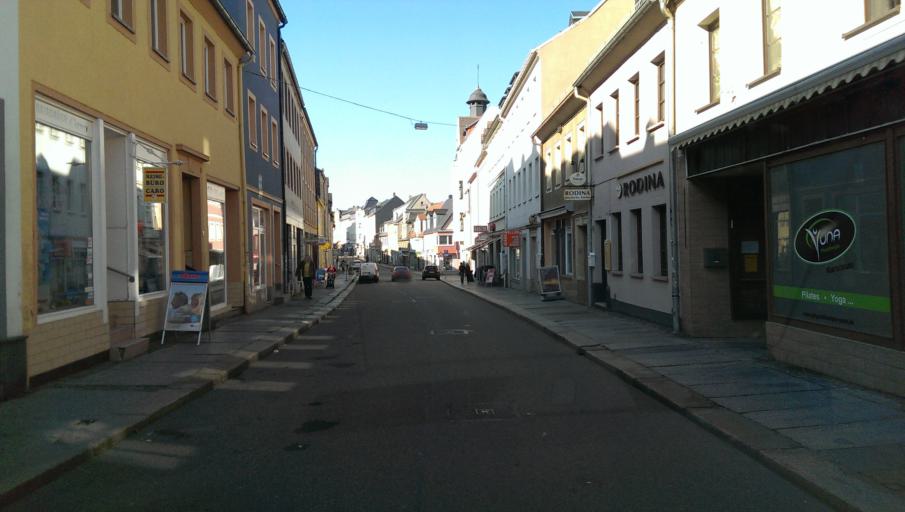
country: DE
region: Saxony
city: Mittweida
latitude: 50.9862
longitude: 12.9784
